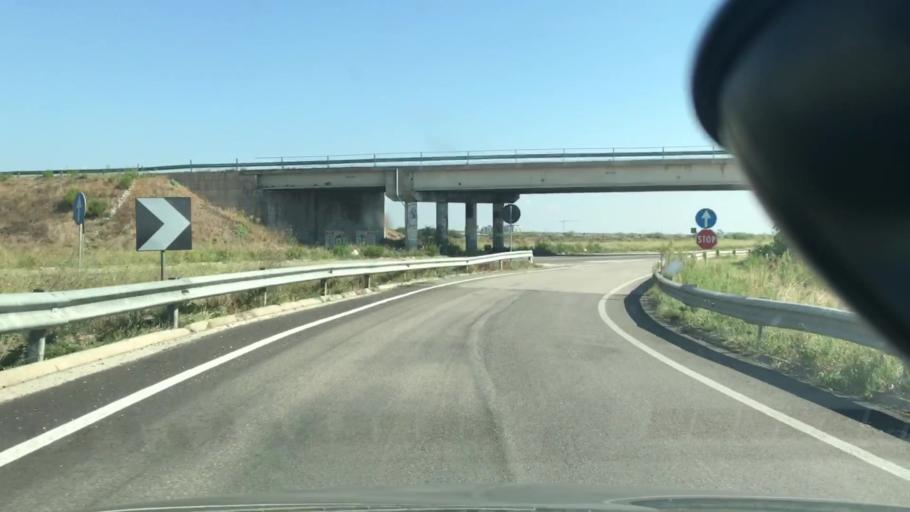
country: IT
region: Apulia
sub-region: Provincia di Foggia
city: Foggia
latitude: 41.4258
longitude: 15.5609
